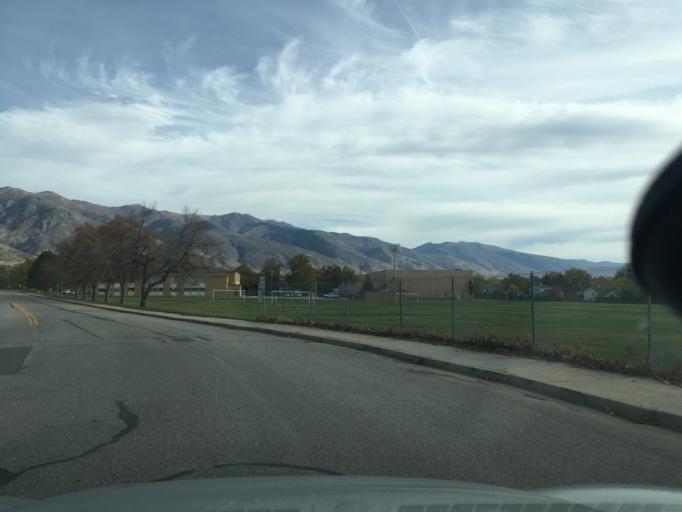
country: US
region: Utah
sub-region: Davis County
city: Layton
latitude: 41.0703
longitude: -111.9685
